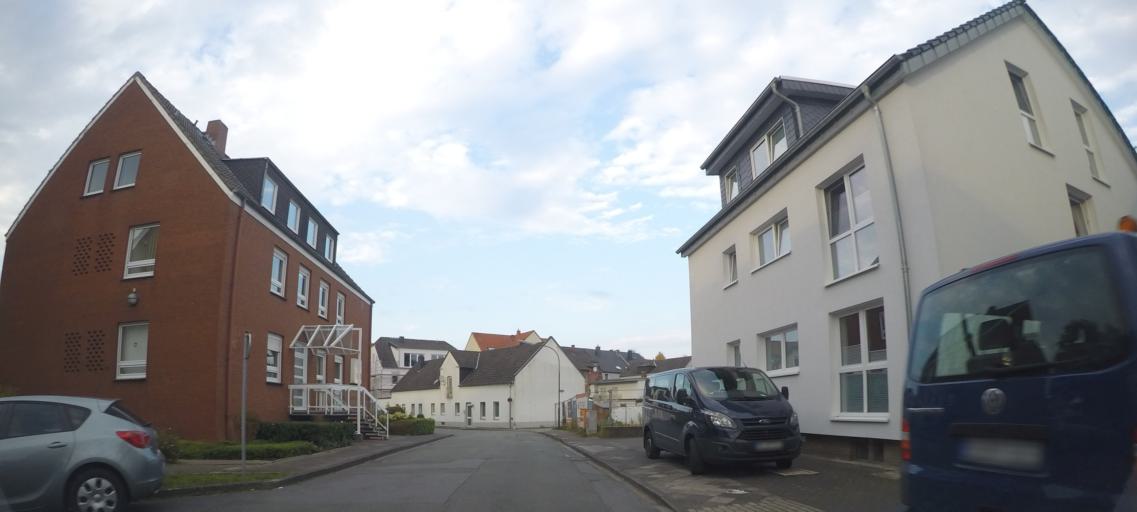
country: DE
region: North Rhine-Westphalia
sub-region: Regierungsbezirk Arnsberg
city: Lippstadt
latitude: 51.6769
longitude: 8.3338
